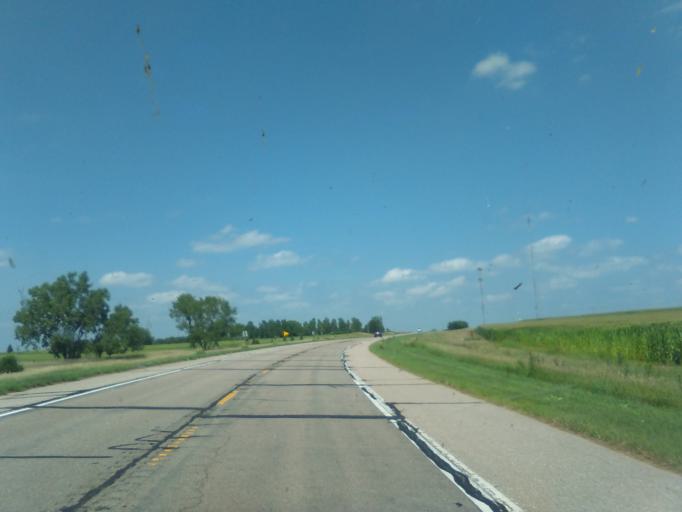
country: US
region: Nebraska
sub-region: Dawson County
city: Lexington
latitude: 40.6968
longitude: -99.7935
